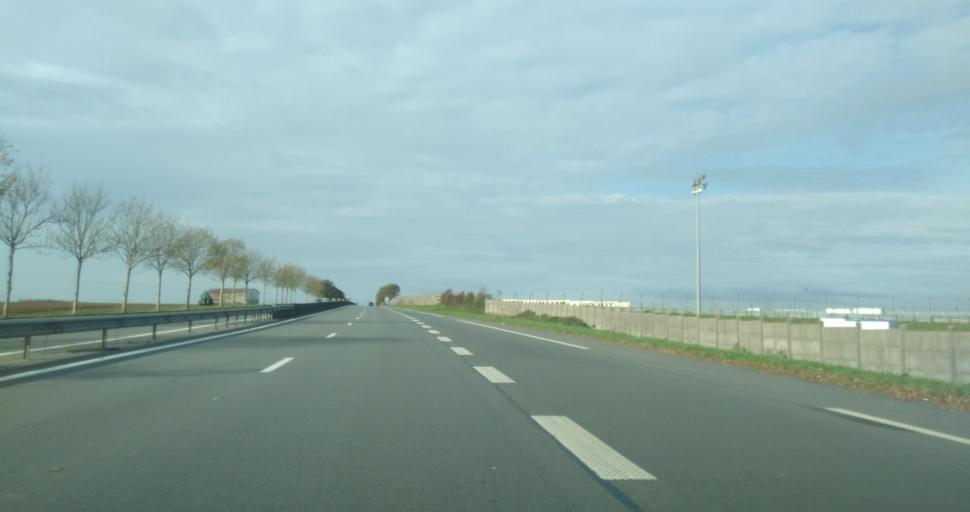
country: FR
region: Nord-Pas-de-Calais
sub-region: Departement du Pas-de-Calais
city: Saint-Pol-sur-Ternoise
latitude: 50.3772
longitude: 2.2951
